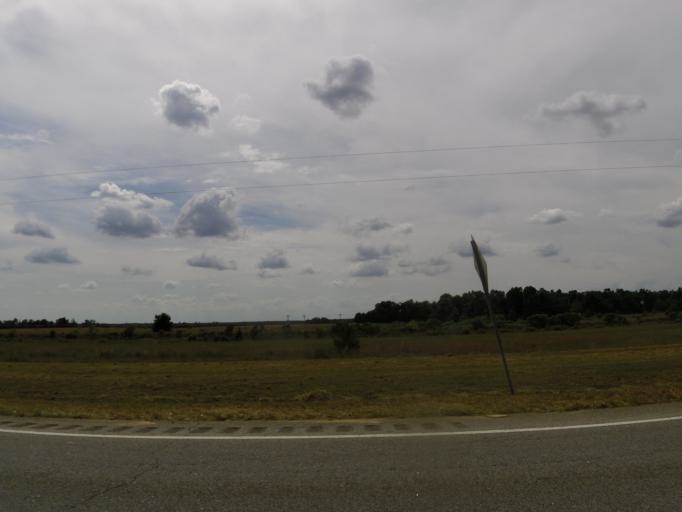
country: US
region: Georgia
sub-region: Jefferson County
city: Louisville
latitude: 33.0820
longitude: -82.4044
